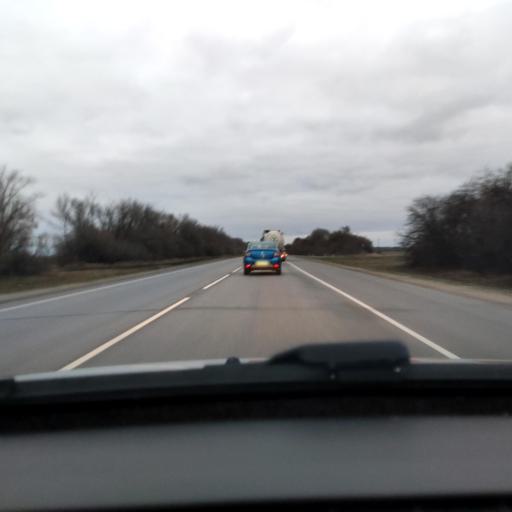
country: RU
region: Lipetsk
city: Borinskoye
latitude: 52.4476
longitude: 39.2909
